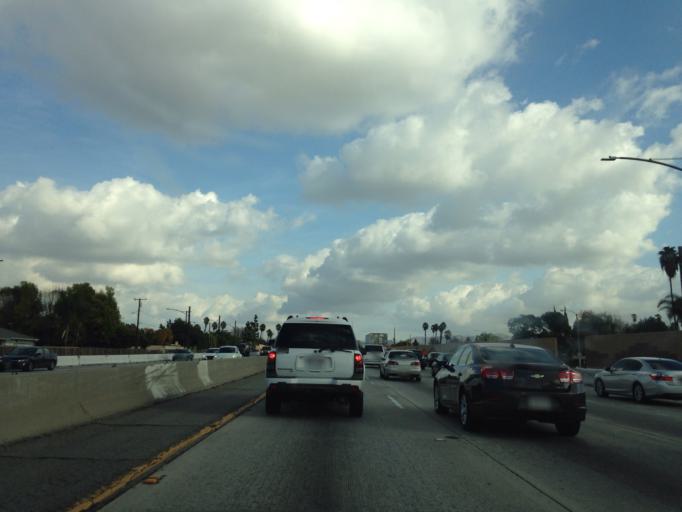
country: US
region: California
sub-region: Los Angeles County
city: West Covina
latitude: 34.0722
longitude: -117.9214
